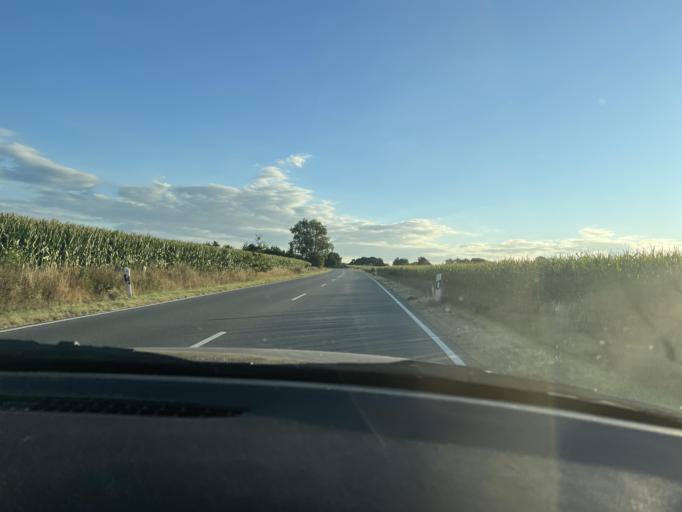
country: DE
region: Schleswig-Holstein
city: Linden
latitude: 54.2517
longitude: 9.1740
